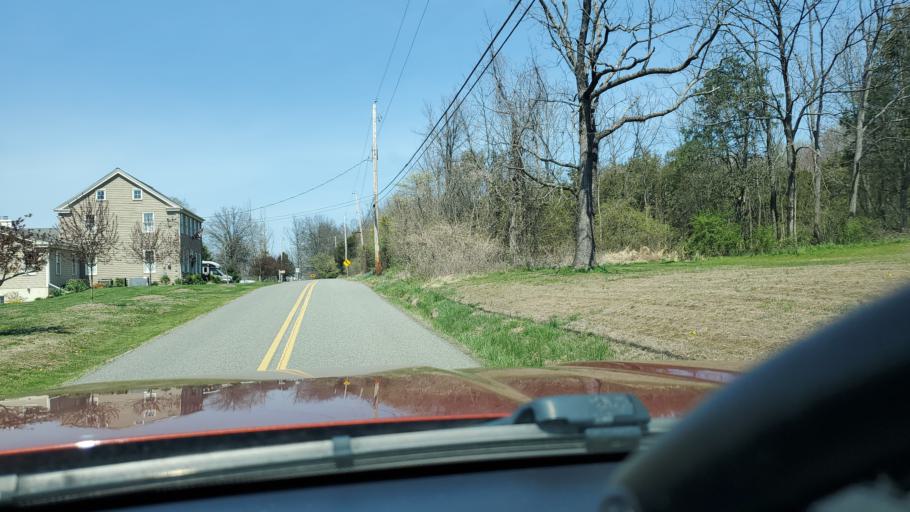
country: US
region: Pennsylvania
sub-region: Montgomery County
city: Gilbertsville
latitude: 40.3320
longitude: -75.5440
